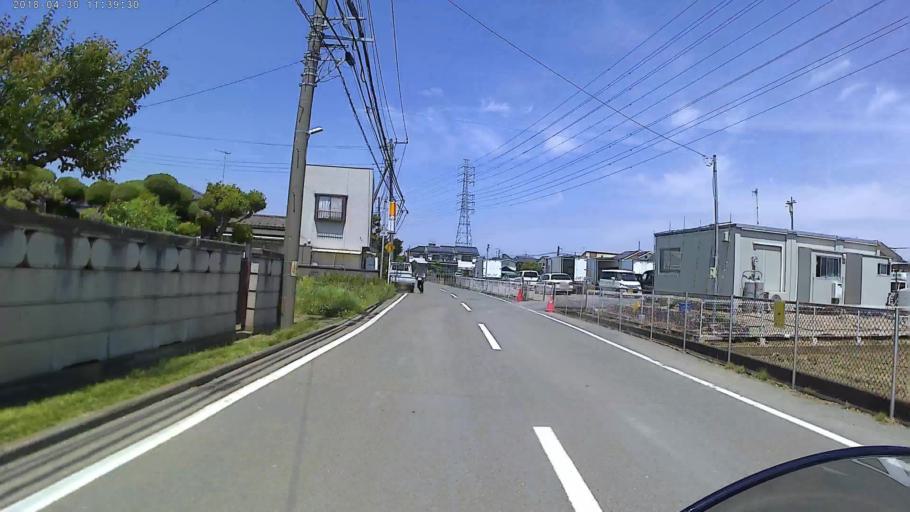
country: JP
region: Kanagawa
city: Zama
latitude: 35.4816
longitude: 139.3894
